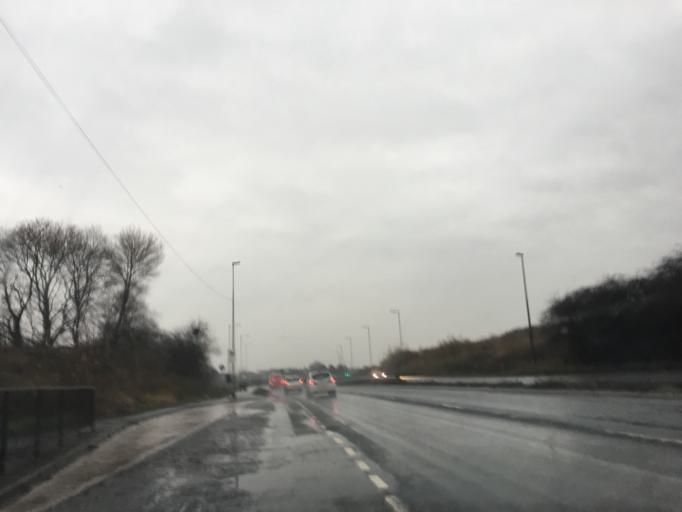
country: GB
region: England
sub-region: Trafford
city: Carrington
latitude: 53.4689
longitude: -2.3871
